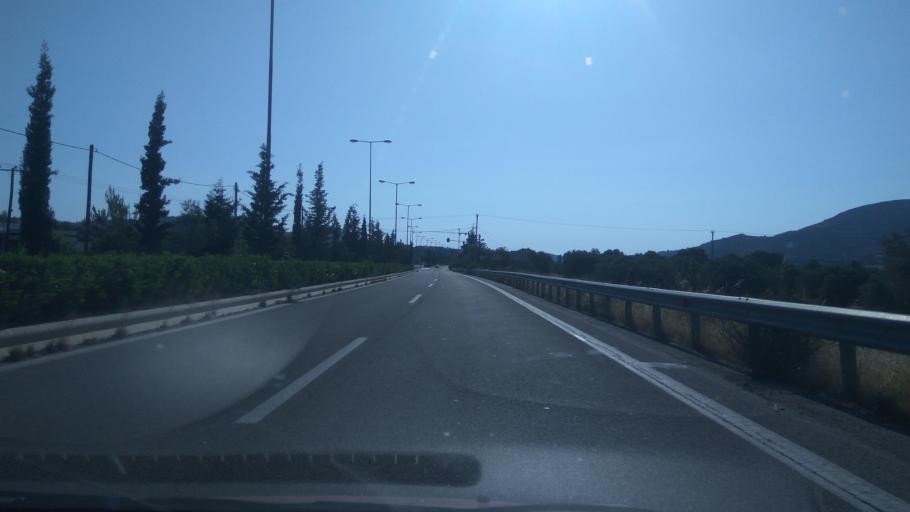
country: GR
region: Attica
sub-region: Nomarchia Anatolikis Attikis
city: Keratea
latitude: 37.8001
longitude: 24.0060
